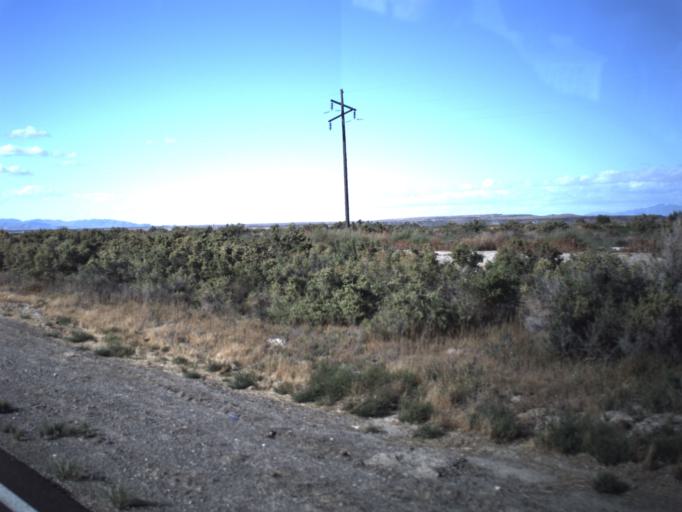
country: US
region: Utah
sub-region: Millard County
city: Delta
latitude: 39.2551
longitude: -112.6537
